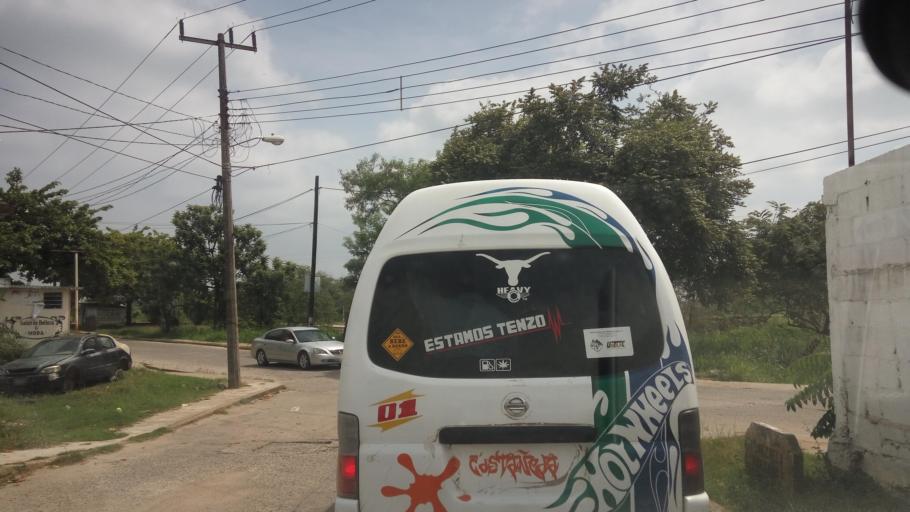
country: MX
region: Chiapas
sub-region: Reforma
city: El Carmen (El Limon)
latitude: 17.8701
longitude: -93.1491
